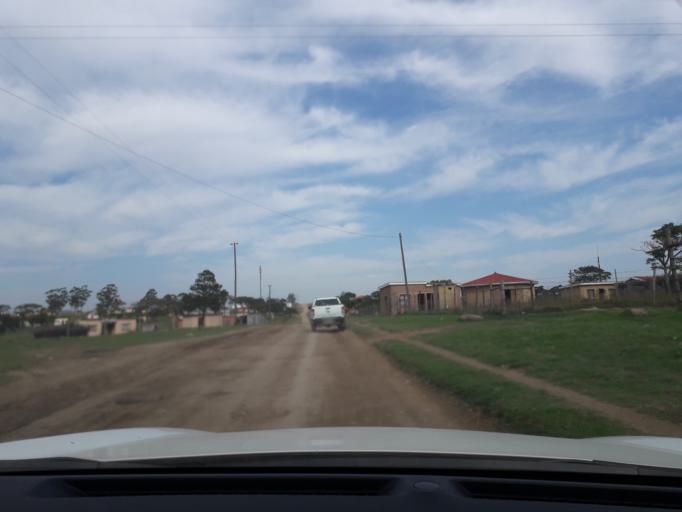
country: ZA
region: Eastern Cape
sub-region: Buffalo City Metropolitan Municipality
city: Bhisho
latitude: -32.9883
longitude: 27.3597
